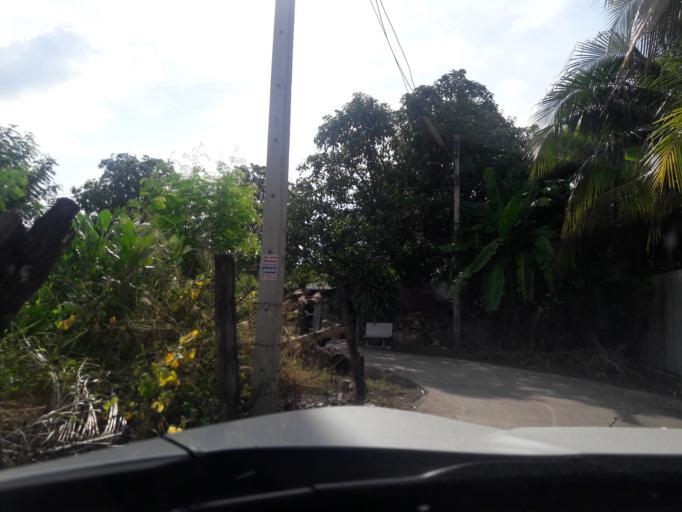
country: TH
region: Lop Buri
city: Ban Mi
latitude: 15.0499
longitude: 100.5484
